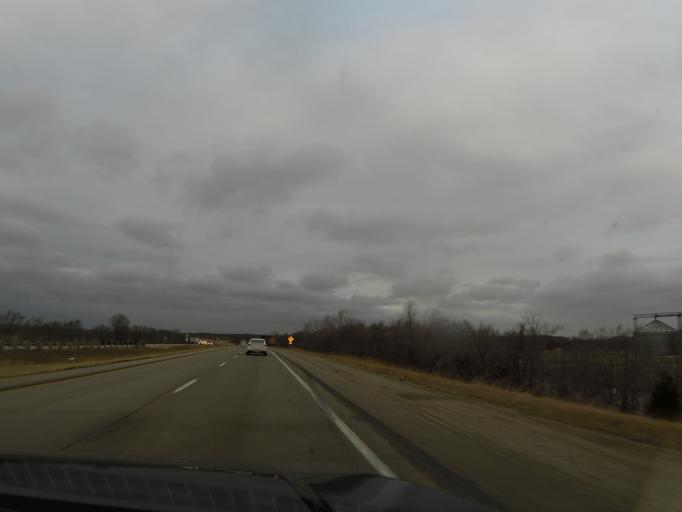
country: US
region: Iowa
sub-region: Black Hawk County
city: Cedar Falls
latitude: 42.5485
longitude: -92.4241
